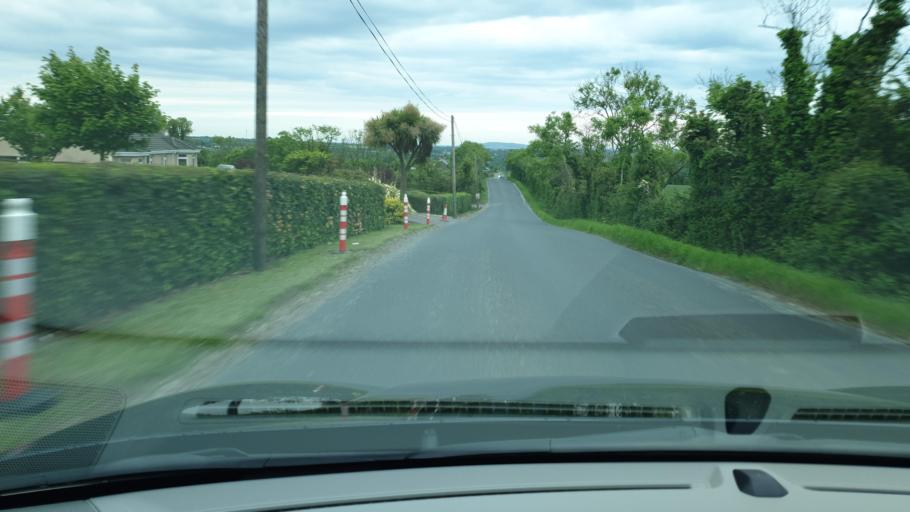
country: IE
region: Leinster
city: Balrothery
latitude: 53.5534
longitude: -6.2407
